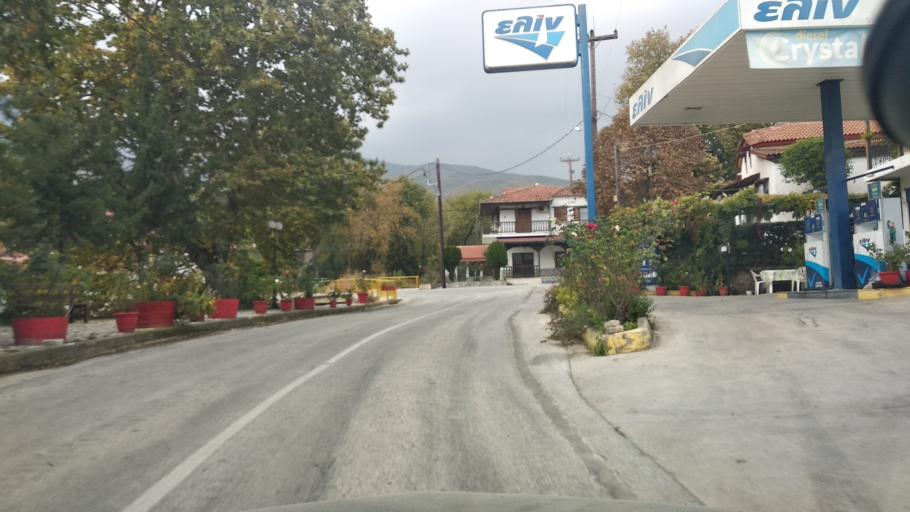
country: GR
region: Thessaly
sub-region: Trikala
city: Kastraki
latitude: 39.6928
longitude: 21.5195
